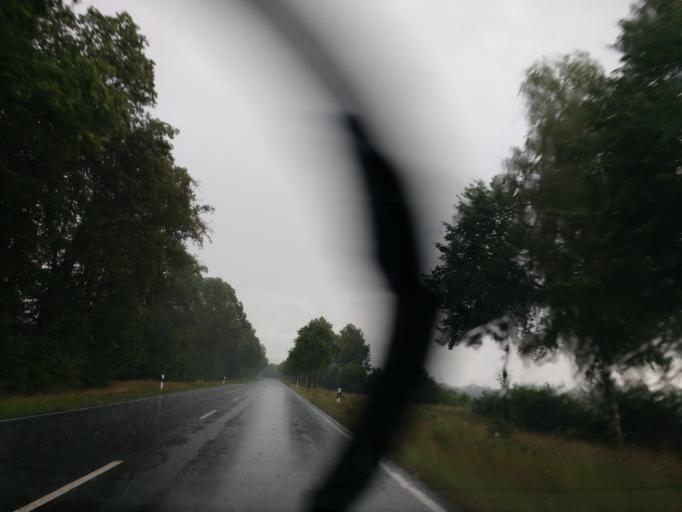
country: DE
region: North Rhine-Westphalia
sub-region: Regierungsbezirk Munster
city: Ostbevern
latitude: 52.1177
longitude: 7.8354
